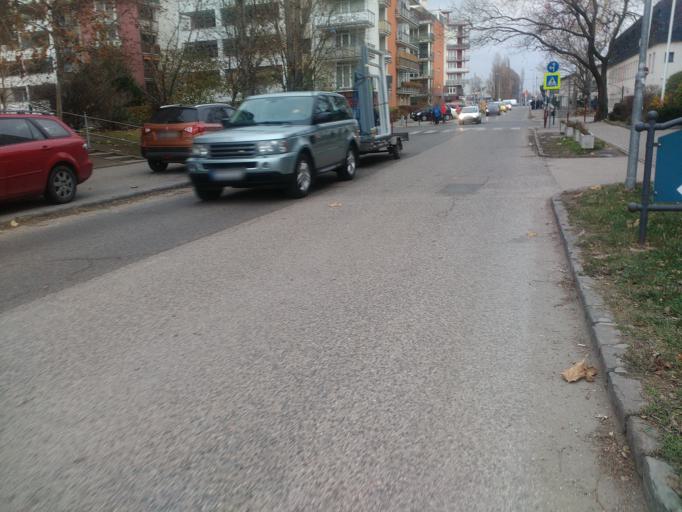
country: HU
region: Budapest
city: Budapest XI. keruelet
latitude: 47.4667
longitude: 19.0468
